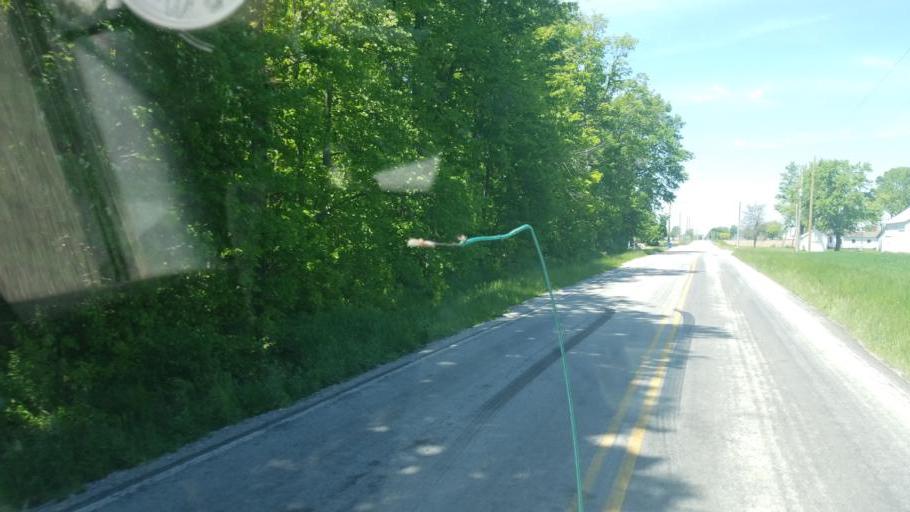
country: US
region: Ohio
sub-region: Huron County
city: Norwalk
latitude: 41.1750
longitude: -82.5392
